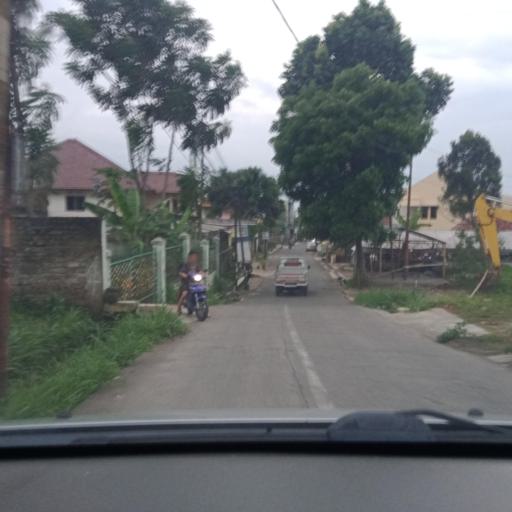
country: ID
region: West Java
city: Cimahi
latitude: -6.8481
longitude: 107.5821
